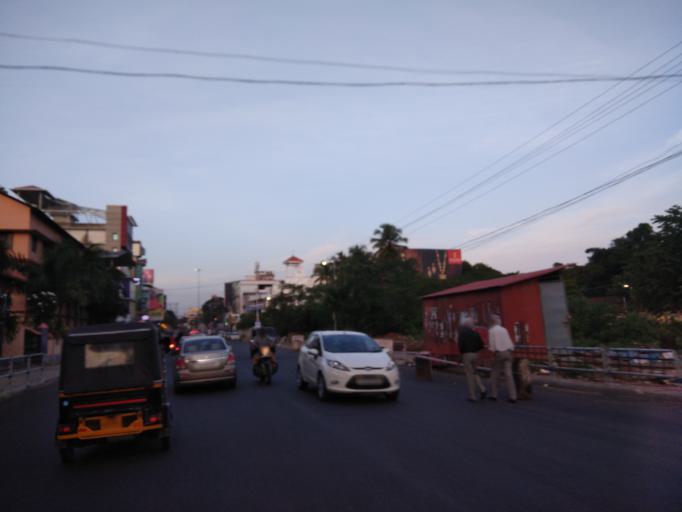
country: IN
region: Kerala
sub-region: Thrissur District
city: Trichur
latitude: 10.5221
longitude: 76.1997
